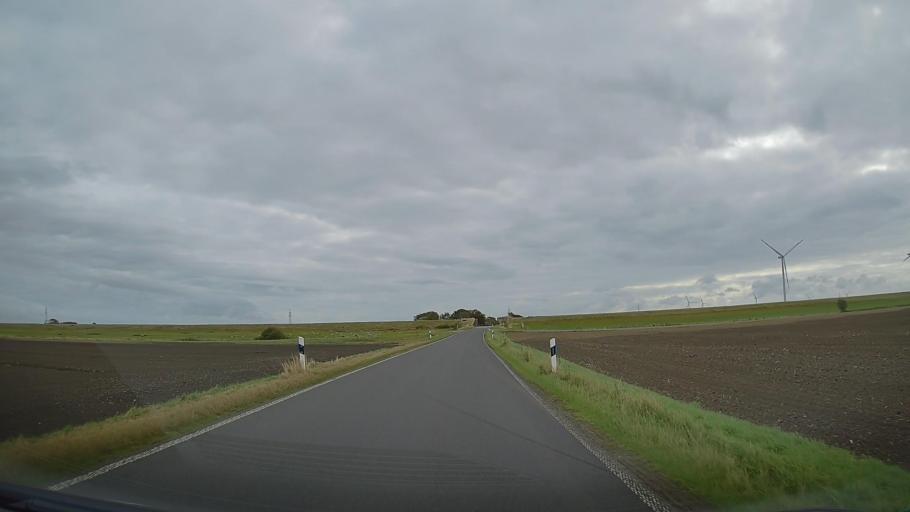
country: DE
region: Schleswig-Holstein
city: Friedrich-Wilhelm-Lubke-Koog
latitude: 54.8685
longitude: 8.6433
